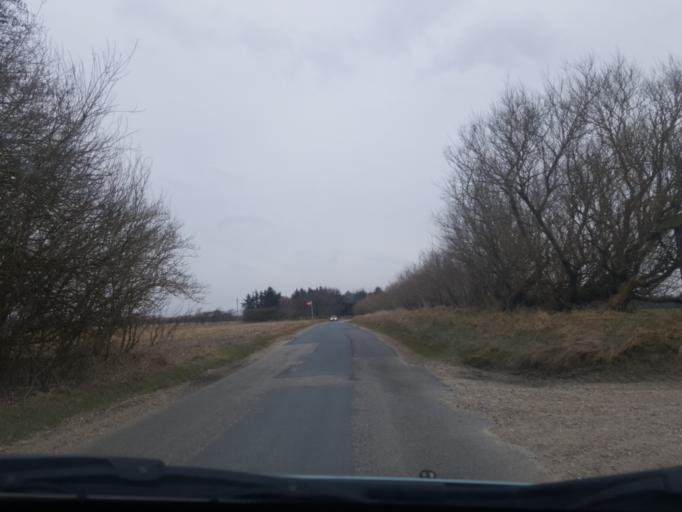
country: DK
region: Central Jutland
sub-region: Holstebro Kommune
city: Ulfborg
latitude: 56.2168
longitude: 8.2622
